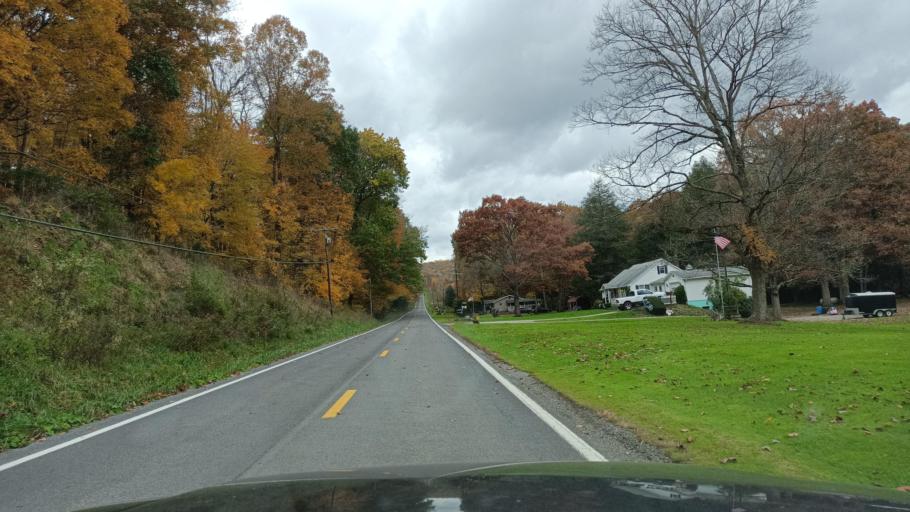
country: US
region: West Virginia
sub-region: Monongalia County
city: Cheat Lake
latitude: 39.6518
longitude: -79.7239
